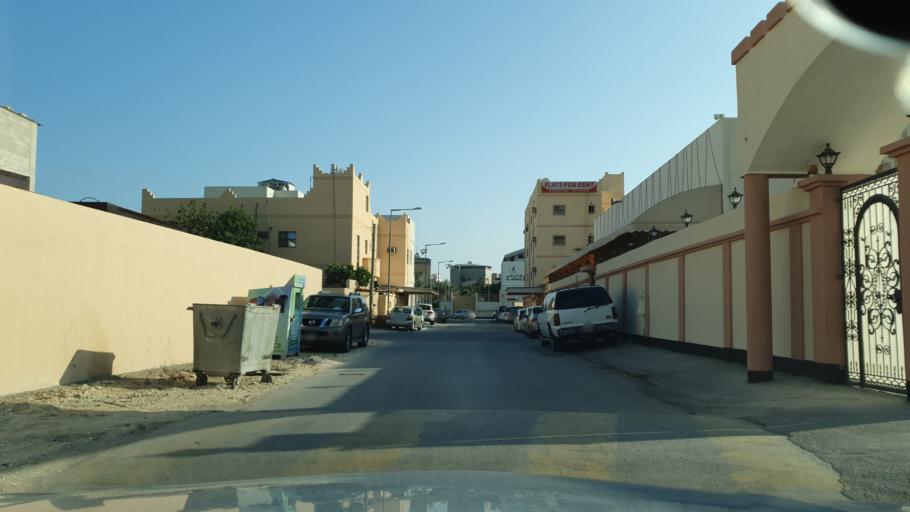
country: BH
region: Manama
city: Jidd Hafs
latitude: 26.2226
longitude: 50.4619
